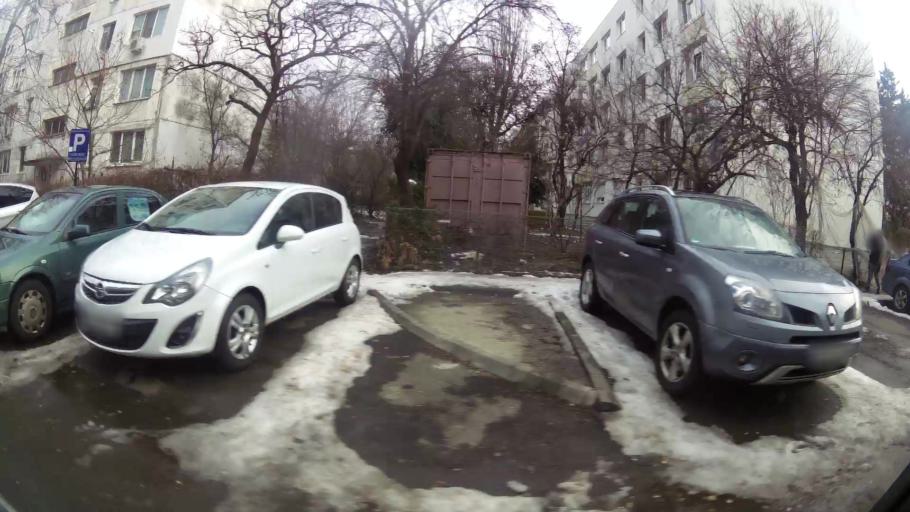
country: RO
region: Ilfov
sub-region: Comuna Popesti-Leordeni
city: Popesti-Leordeni
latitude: 44.4072
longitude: 26.1725
